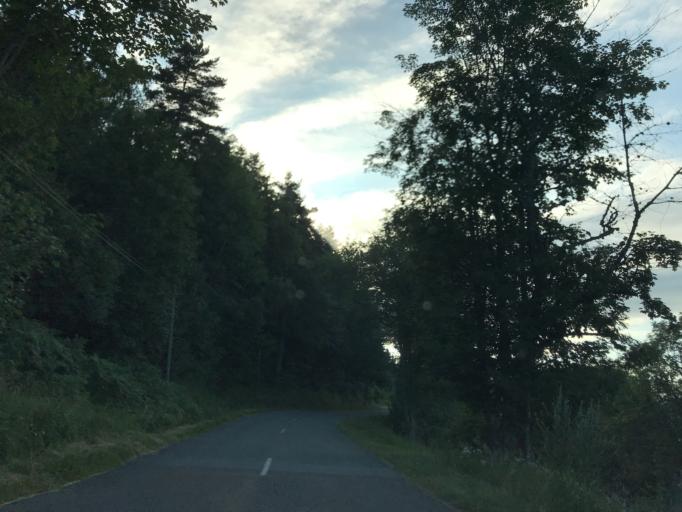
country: FR
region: Rhone-Alpes
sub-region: Departement de la Loire
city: Sail-sous-Couzan
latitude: 45.7427
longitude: 3.8582
